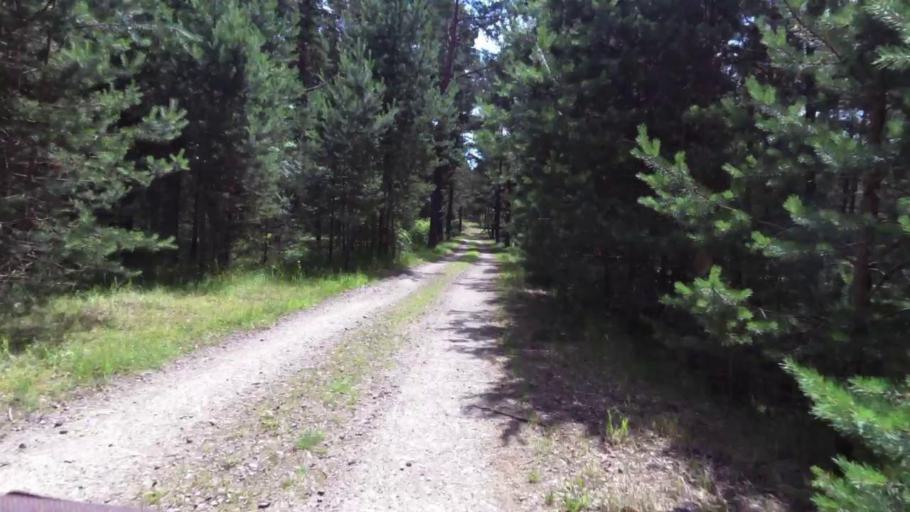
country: PL
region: West Pomeranian Voivodeship
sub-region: Powiat gryficki
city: Mrzezyno
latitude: 54.1251
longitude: 15.2216
